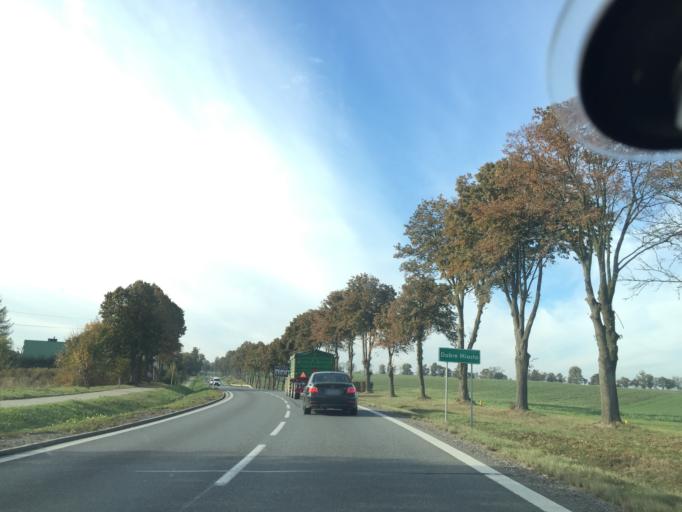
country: PL
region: Warmian-Masurian Voivodeship
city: Dobre Miasto
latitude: 53.9990
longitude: 20.4021
